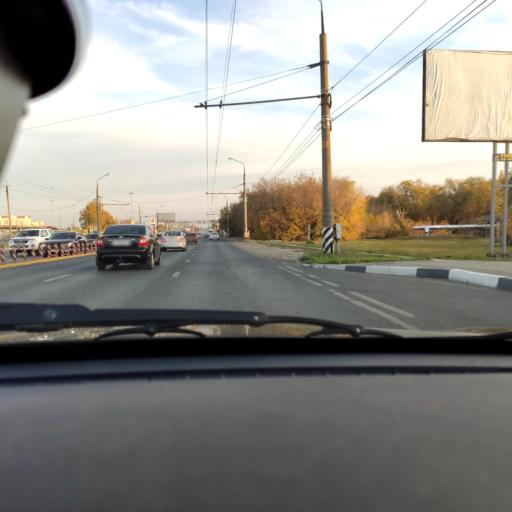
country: RU
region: Samara
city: Tol'yatti
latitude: 53.5428
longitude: 49.3838
